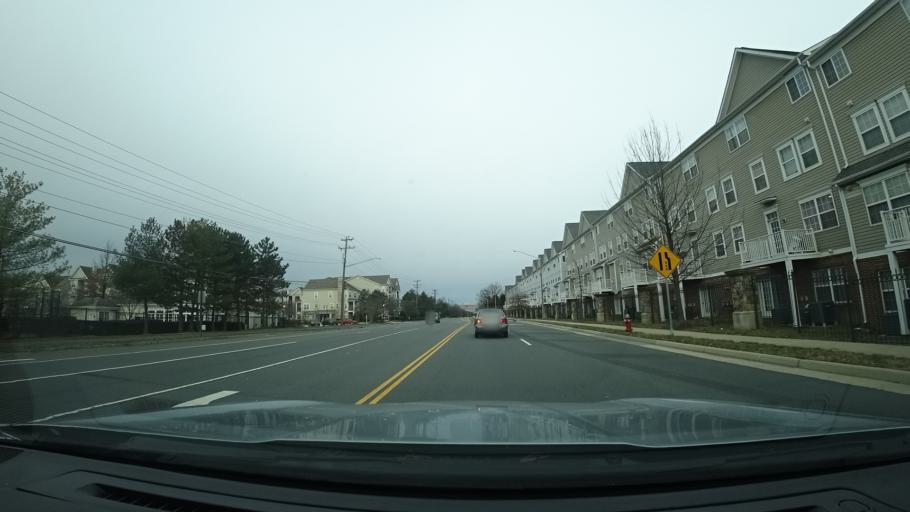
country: US
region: Virginia
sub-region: Fairfax County
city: Floris
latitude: 38.9492
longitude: -77.4165
